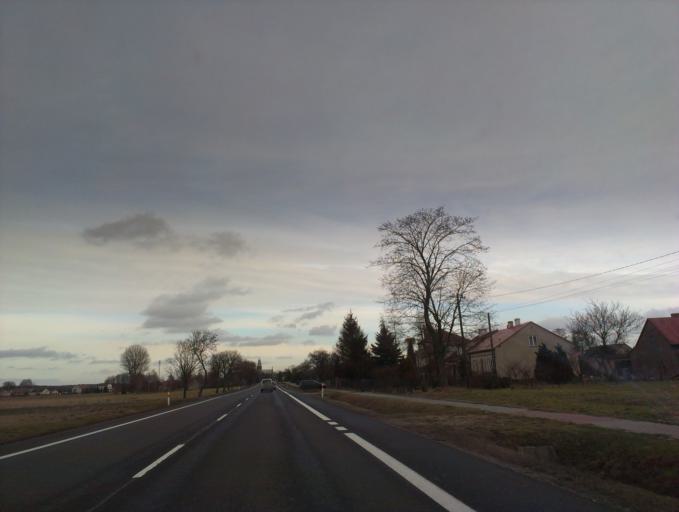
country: PL
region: Masovian Voivodeship
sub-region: Powiat sierpecki
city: Szczutowo
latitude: 52.9025
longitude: 19.5125
